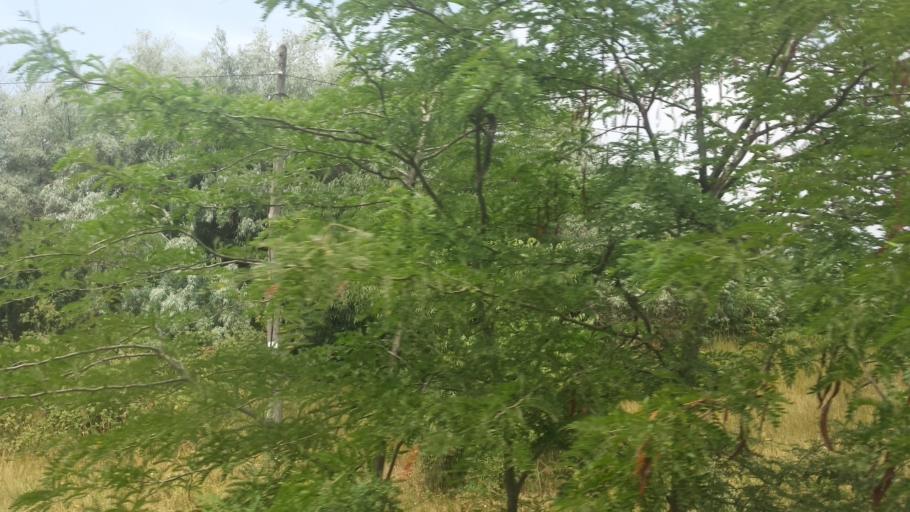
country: RO
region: Constanta
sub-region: Comuna Navodari
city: Navodari
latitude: 44.3254
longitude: 28.6199
